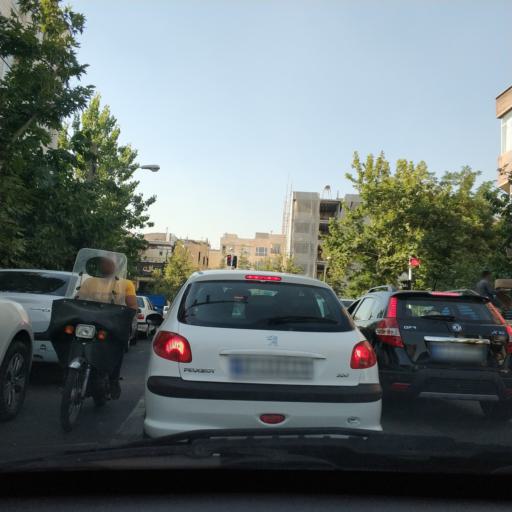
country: IR
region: Tehran
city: Tehran
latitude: 35.7204
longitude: 51.4853
